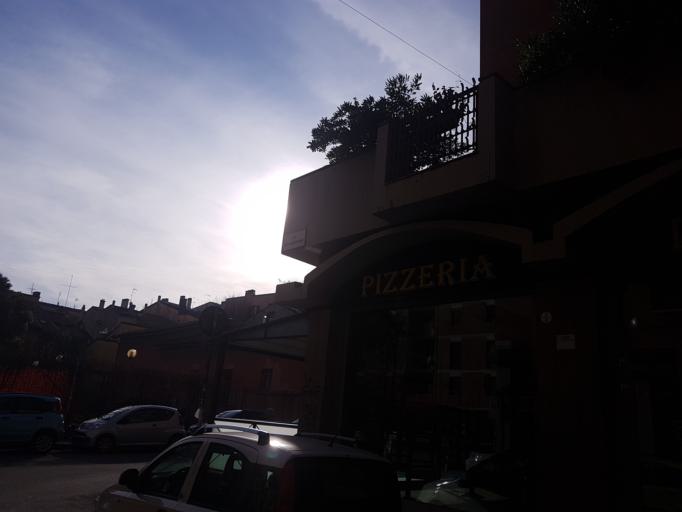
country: IT
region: Emilia-Romagna
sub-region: Provincia di Bologna
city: Bologna
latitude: 44.4965
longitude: 11.3300
